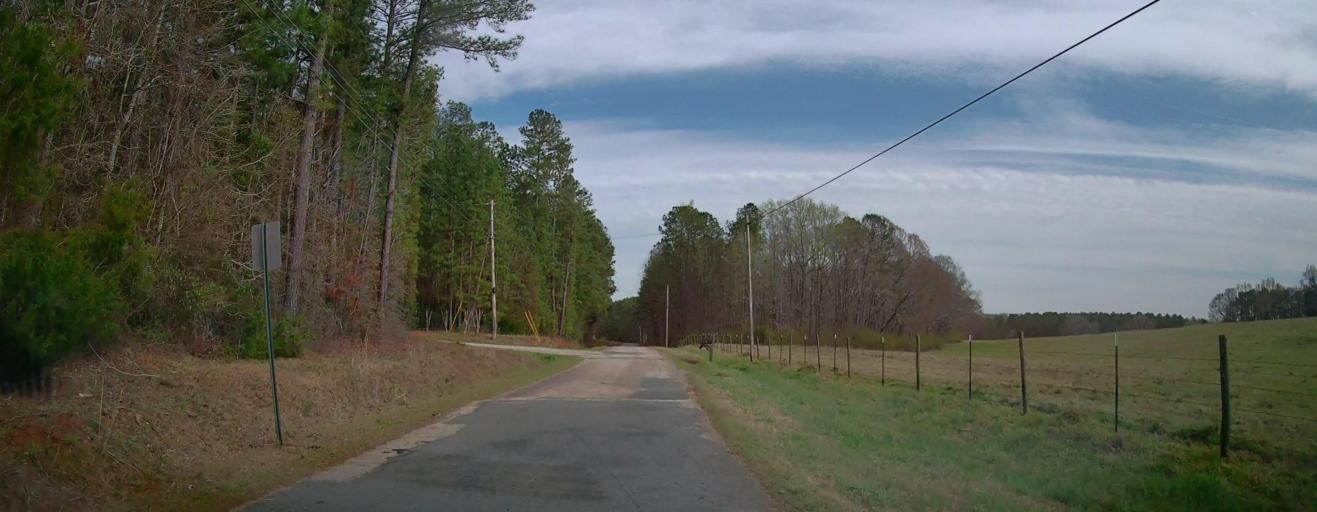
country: US
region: Georgia
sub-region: Monroe County
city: Forsyth
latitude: 33.0423
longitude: -83.8957
